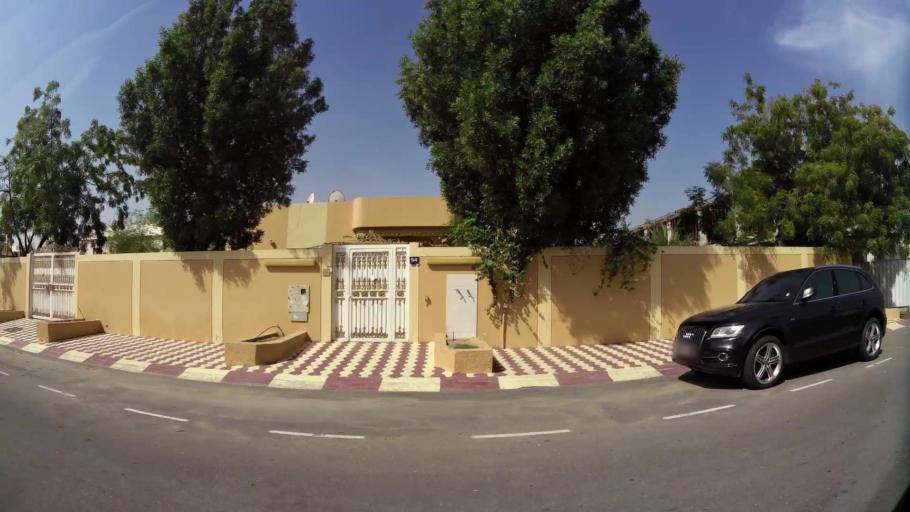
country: AE
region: Ash Shariqah
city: Sharjah
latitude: 25.2707
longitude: 55.4084
